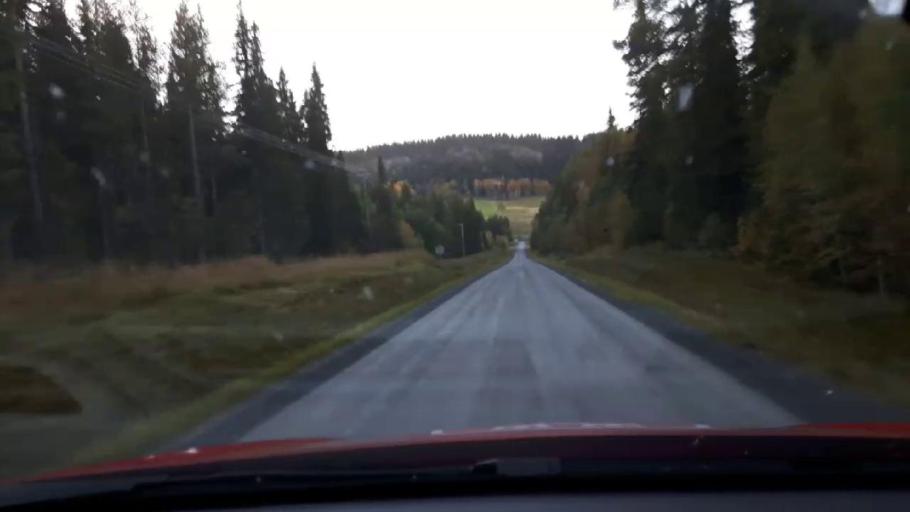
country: SE
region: Jaemtland
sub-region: Krokoms Kommun
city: Krokom
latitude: 63.4832
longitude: 14.2079
